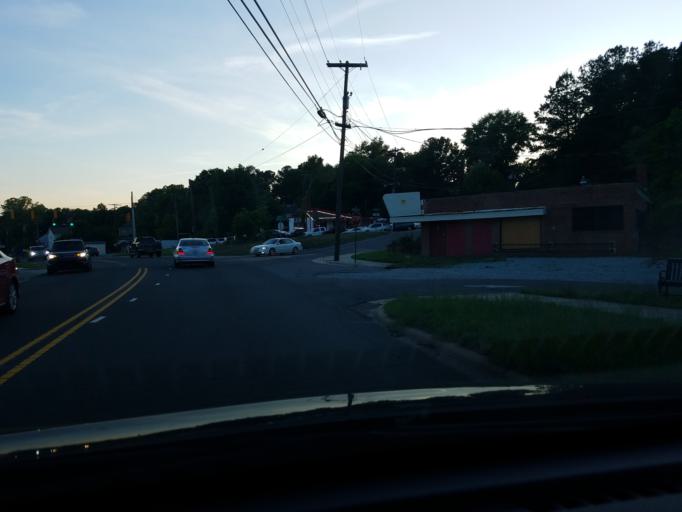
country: US
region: North Carolina
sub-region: Durham County
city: Durham
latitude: 35.9867
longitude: -78.9085
